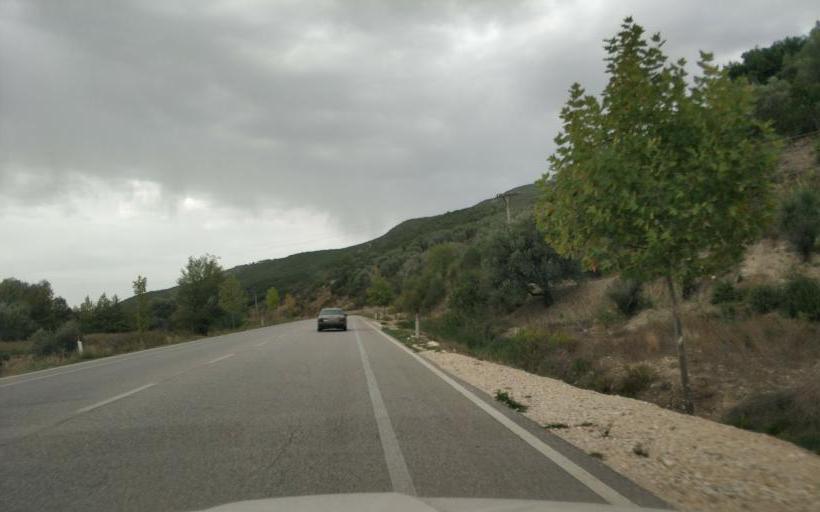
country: AL
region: Fier
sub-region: Rrethi i Mallakastres
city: Hekal
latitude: 40.5231
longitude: 19.7389
